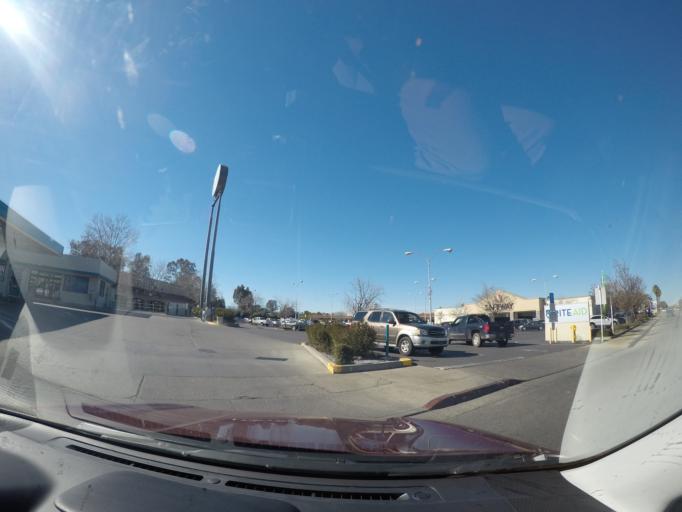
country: US
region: California
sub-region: Tehama County
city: Corning
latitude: 39.9286
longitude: -122.1975
